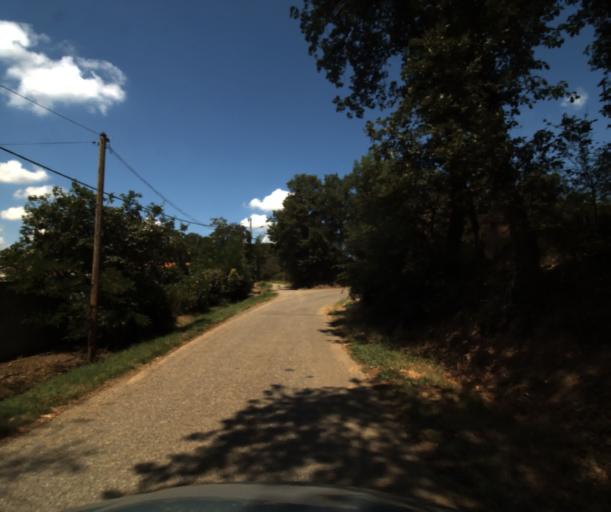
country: FR
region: Midi-Pyrenees
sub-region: Departement de la Haute-Garonne
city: Labastidette
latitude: 43.4700
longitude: 1.2067
